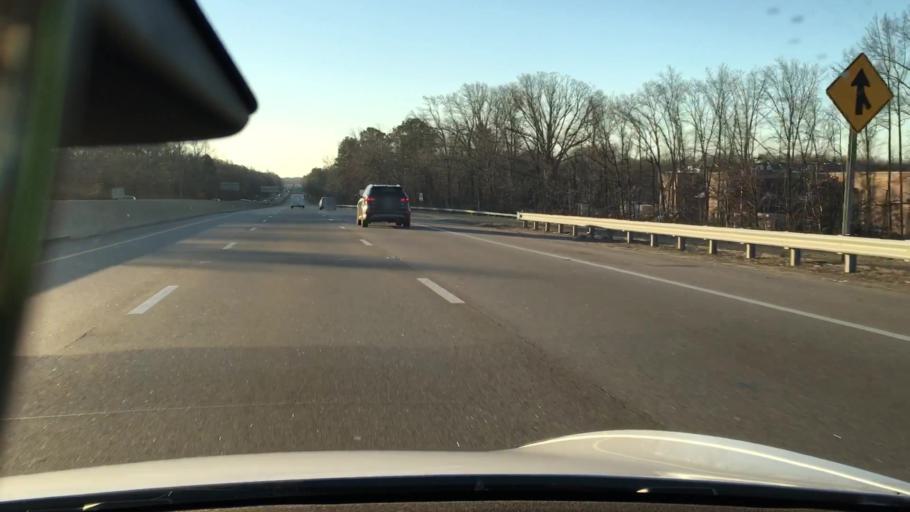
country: US
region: Virginia
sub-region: Chesterfield County
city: Bon Air
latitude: 37.5004
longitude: -77.5245
